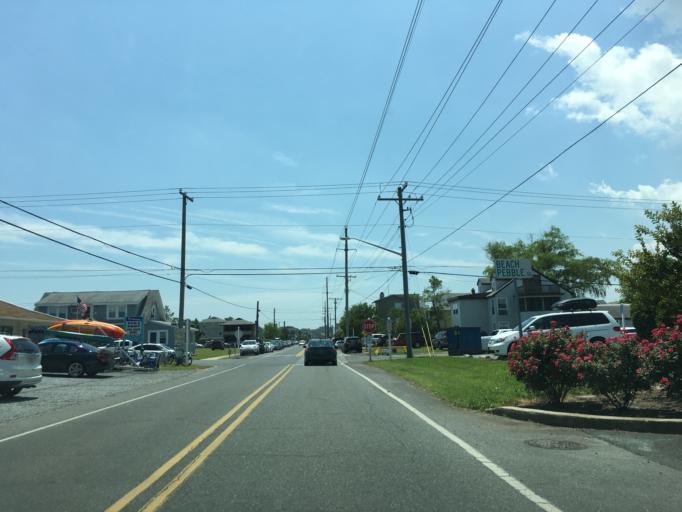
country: US
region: Delaware
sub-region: Sussex County
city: Bethany Beach
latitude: 38.5459
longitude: -75.0583
